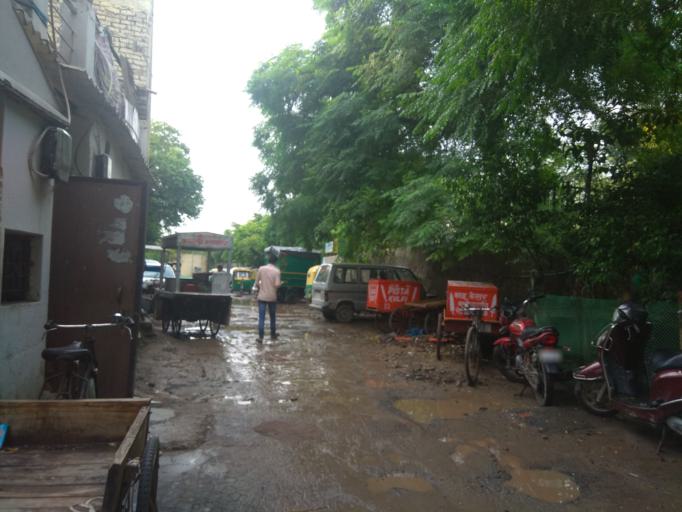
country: IN
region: NCT
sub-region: New Delhi
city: New Delhi
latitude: 28.5719
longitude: 77.2517
